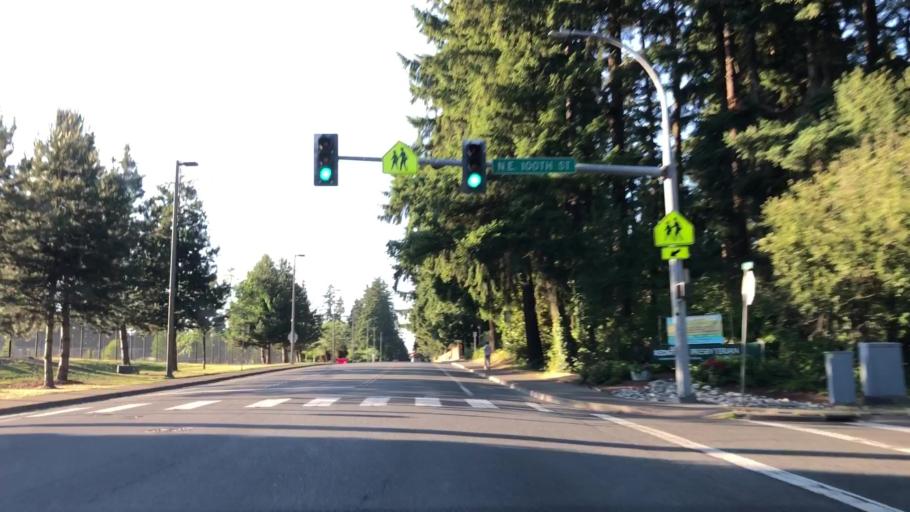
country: US
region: Washington
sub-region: King County
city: Redmond
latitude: 47.6893
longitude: -122.1178
